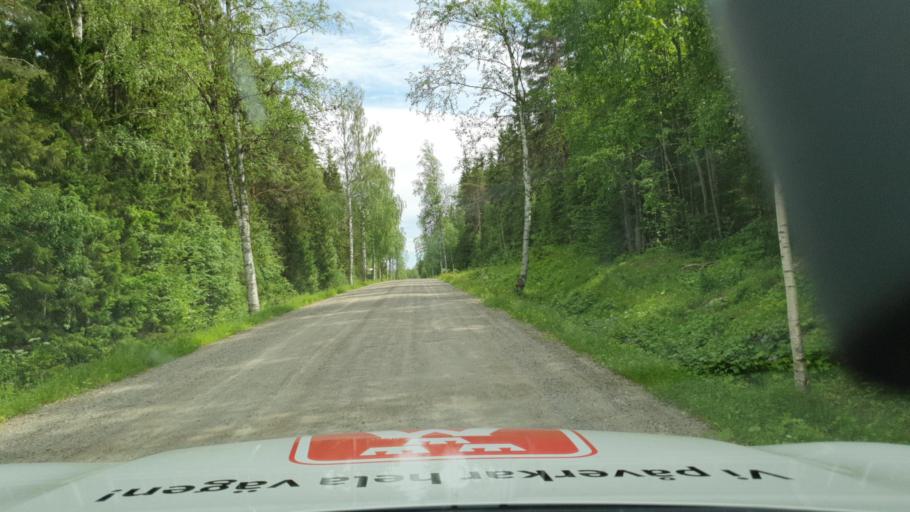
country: SE
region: Vaesterbotten
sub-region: Skelleftea Kommun
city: Burtraesk
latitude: 64.4757
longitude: 20.4438
